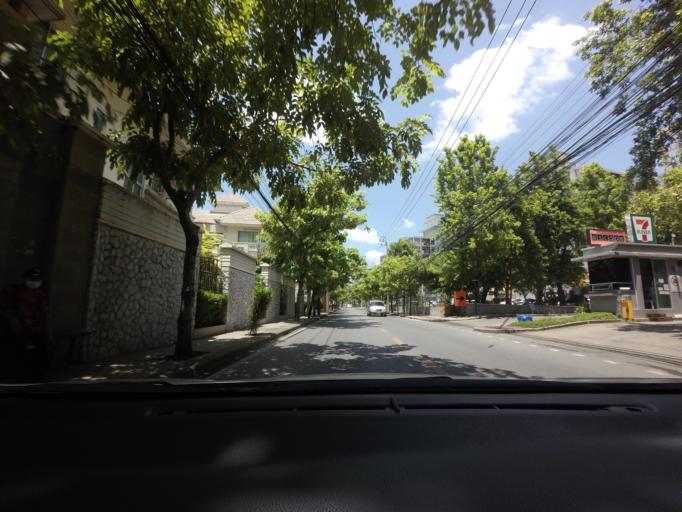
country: TH
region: Bangkok
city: Bang Na
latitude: 13.6879
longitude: 100.6352
